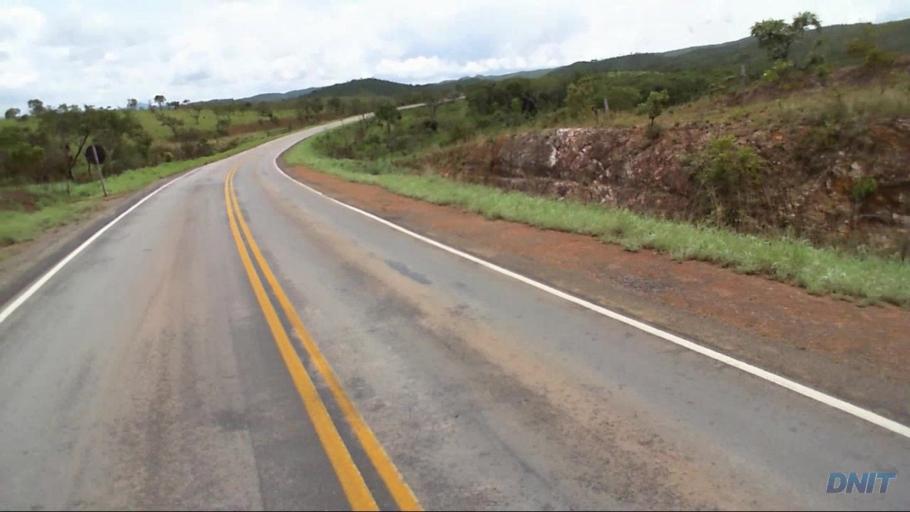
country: BR
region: Goias
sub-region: Padre Bernardo
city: Padre Bernardo
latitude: -15.4660
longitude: -48.2268
